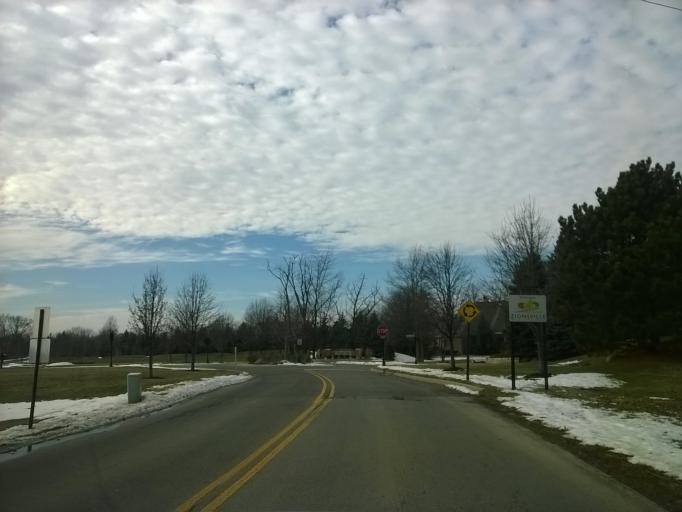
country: US
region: Indiana
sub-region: Boone County
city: Zionsville
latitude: 39.9771
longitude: -86.2408
